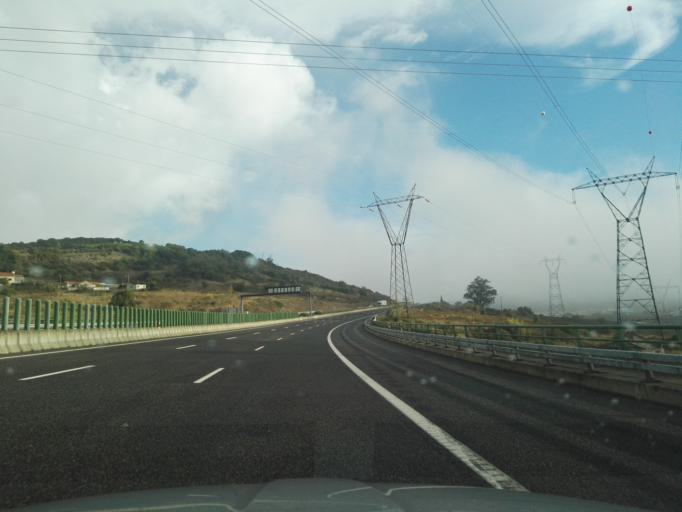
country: PT
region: Lisbon
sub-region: Arruda Dos Vinhos
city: Arruda dos Vinhos
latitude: 38.9506
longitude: -9.0664
